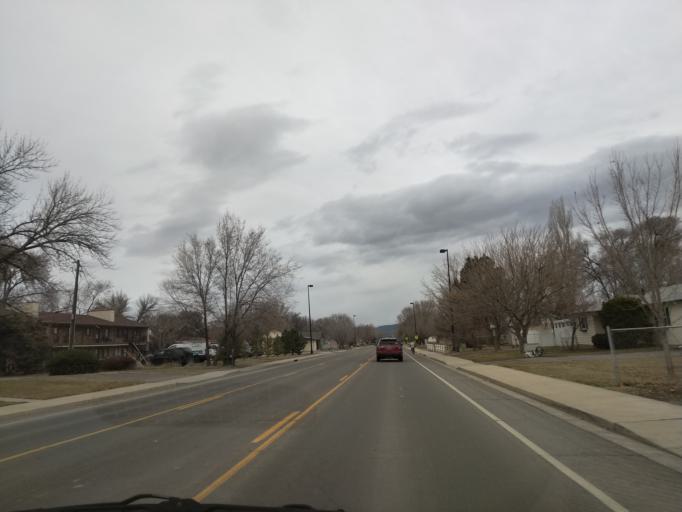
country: US
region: Colorado
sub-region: Mesa County
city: Fruitvale
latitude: 39.0837
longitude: -108.5152
